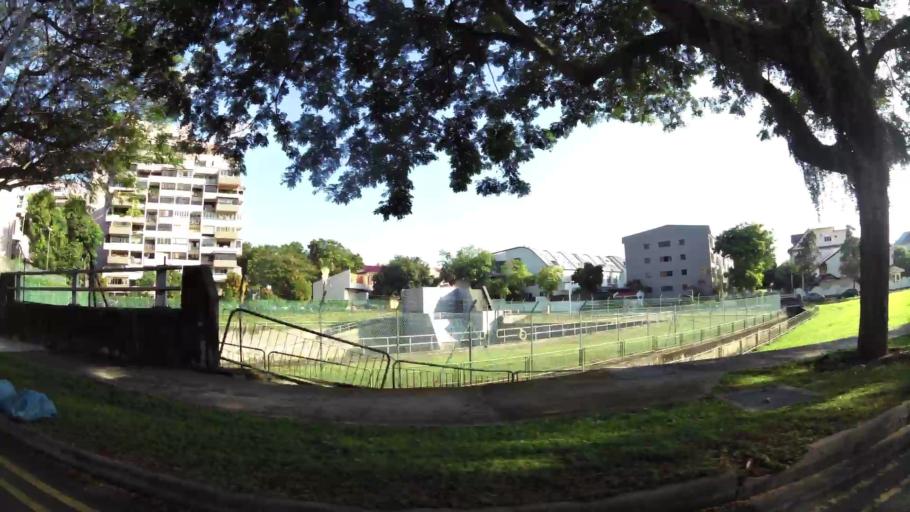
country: SG
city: Singapore
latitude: 1.3212
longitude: 103.9463
